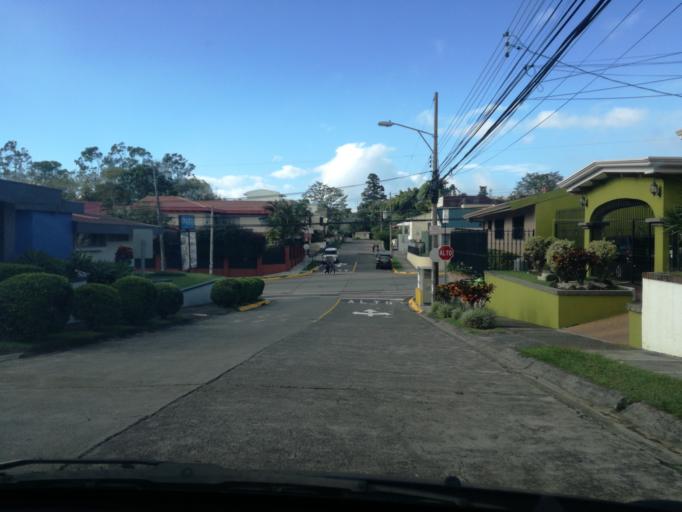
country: CR
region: San Jose
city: San Pedro
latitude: 9.9267
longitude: -84.0440
